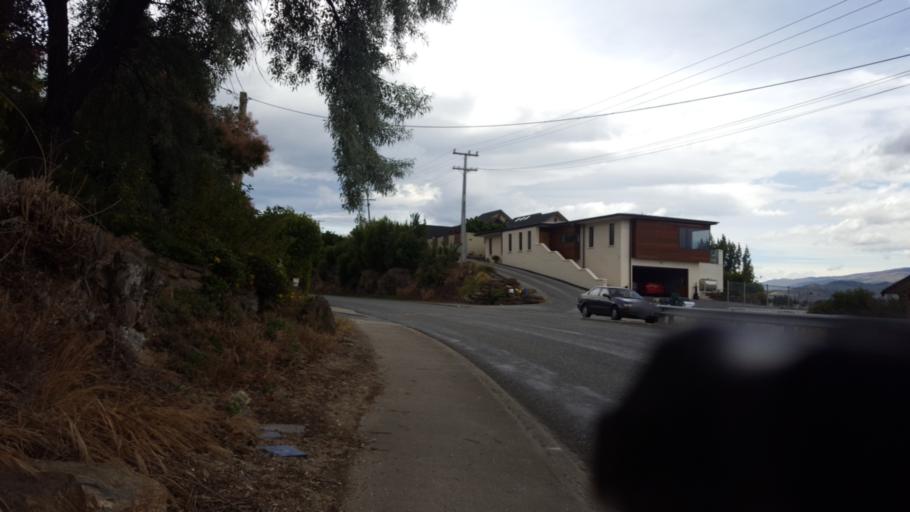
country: NZ
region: Otago
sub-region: Queenstown-Lakes District
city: Wanaka
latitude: -45.2583
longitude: 169.3843
